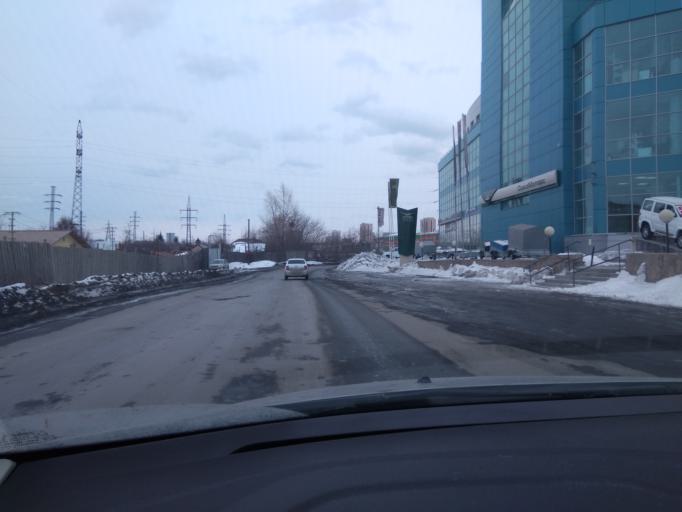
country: RU
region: Sverdlovsk
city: Yekaterinburg
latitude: 56.8740
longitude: 60.6317
